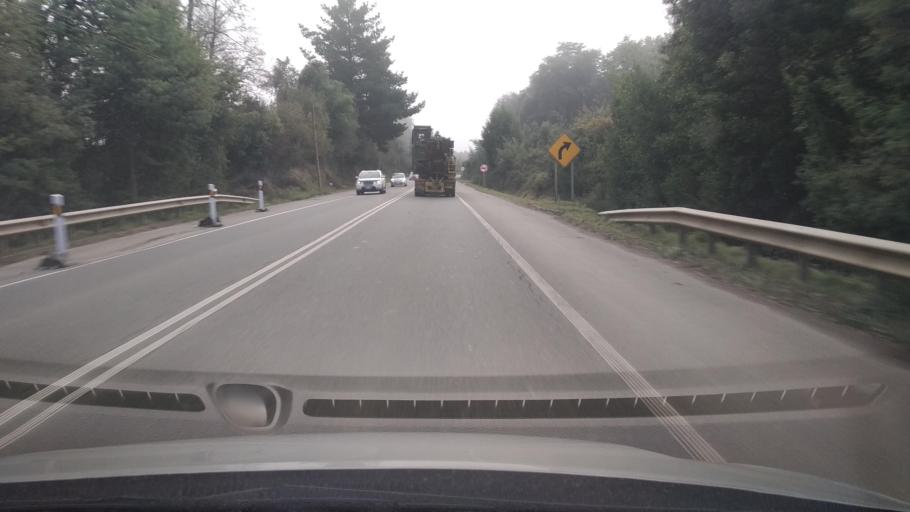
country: CL
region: Los Lagos
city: Las Animas
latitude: -39.7680
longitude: -73.2246
